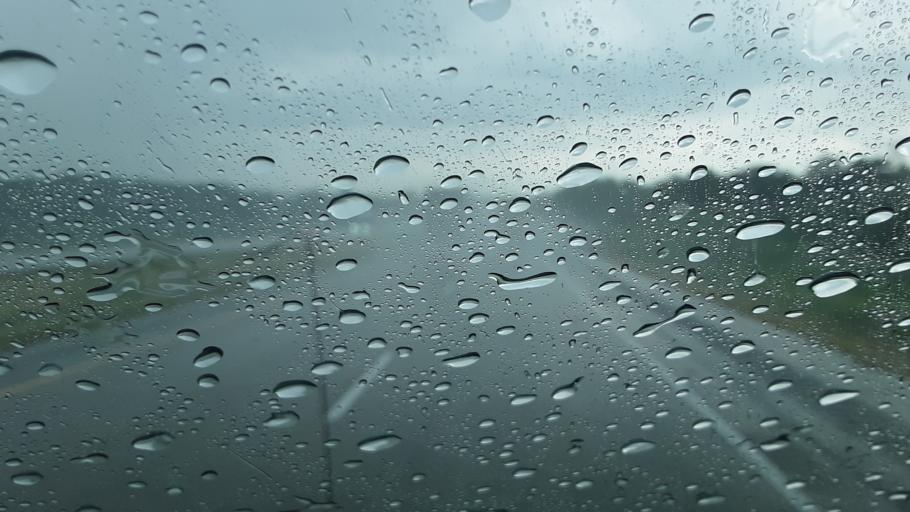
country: US
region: Iowa
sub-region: Pottawattamie County
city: Council Bluffs
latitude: 41.2919
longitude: -95.7769
